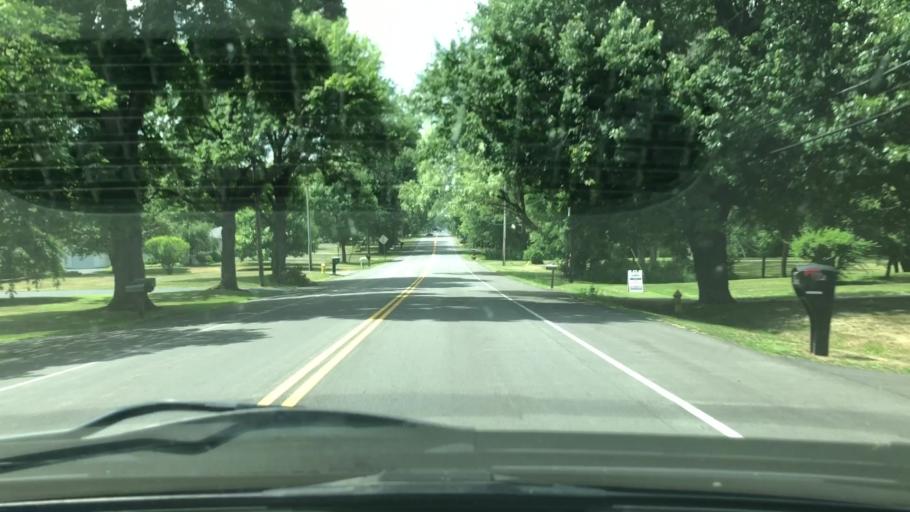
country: US
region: New York
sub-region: Monroe County
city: North Gates
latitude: 43.1255
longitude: -77.7315
